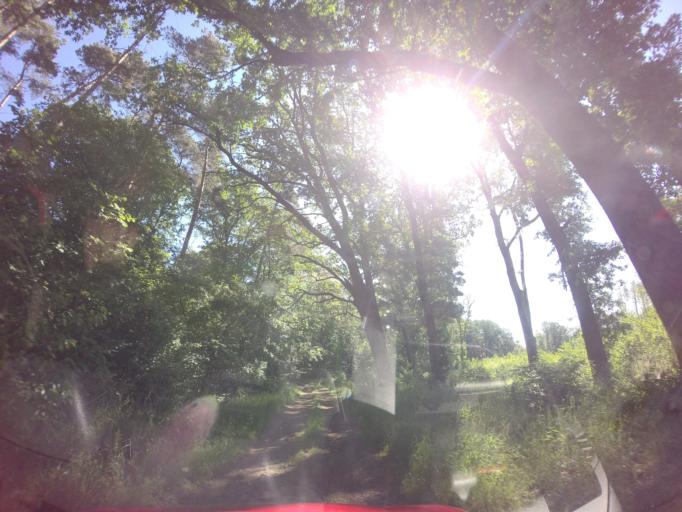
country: PL
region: West Pomeranian Voivodeship
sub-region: Powiat choszczenski
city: Choszczno
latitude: 53.1732
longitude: 15.3535
